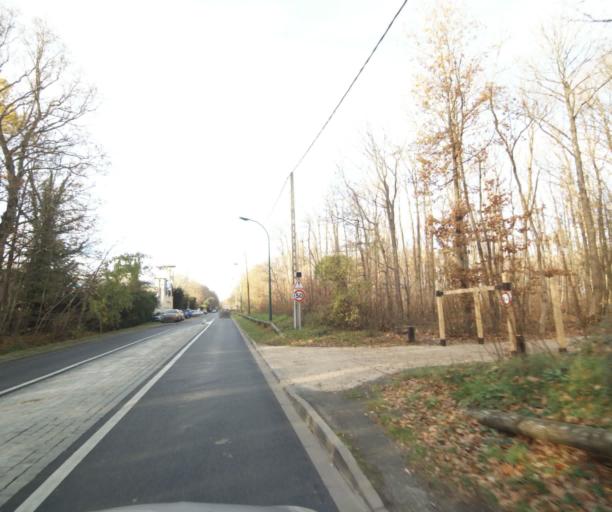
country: FR
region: Ile-de-France
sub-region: Departement du Val-d'Oise
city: Courdimanche
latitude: 49.0113
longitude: 2.0035
